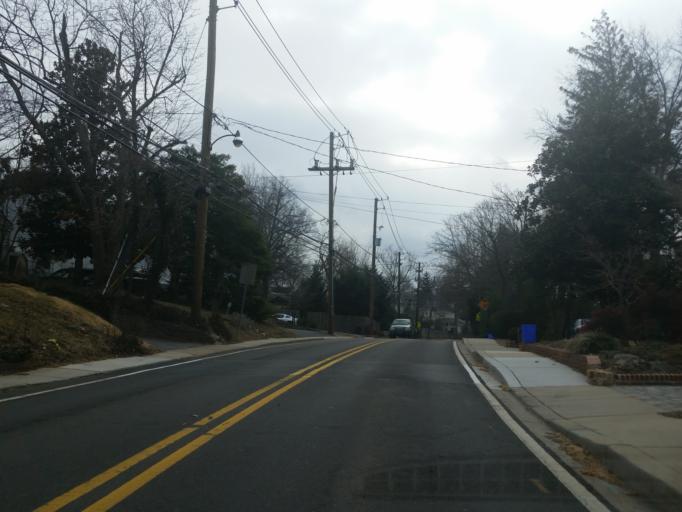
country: US
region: Maryland
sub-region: Montgomery County
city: Chevy Chase
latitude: 38.9792
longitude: -77.0709
